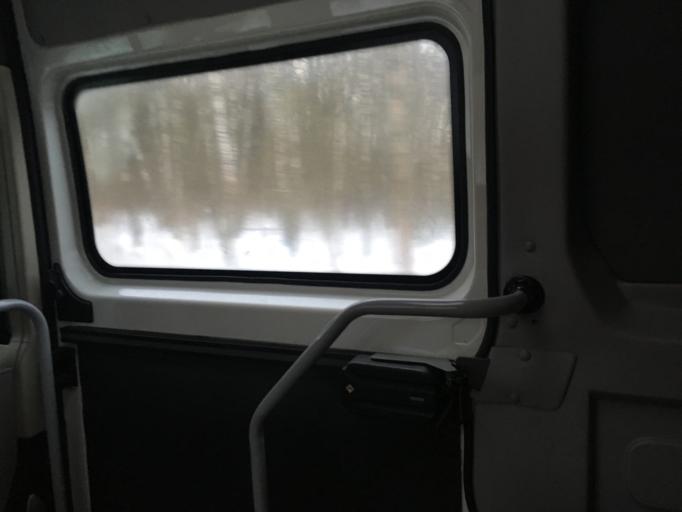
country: RU
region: Tula
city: Krapivna
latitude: 54.1370
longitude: 37.2667
